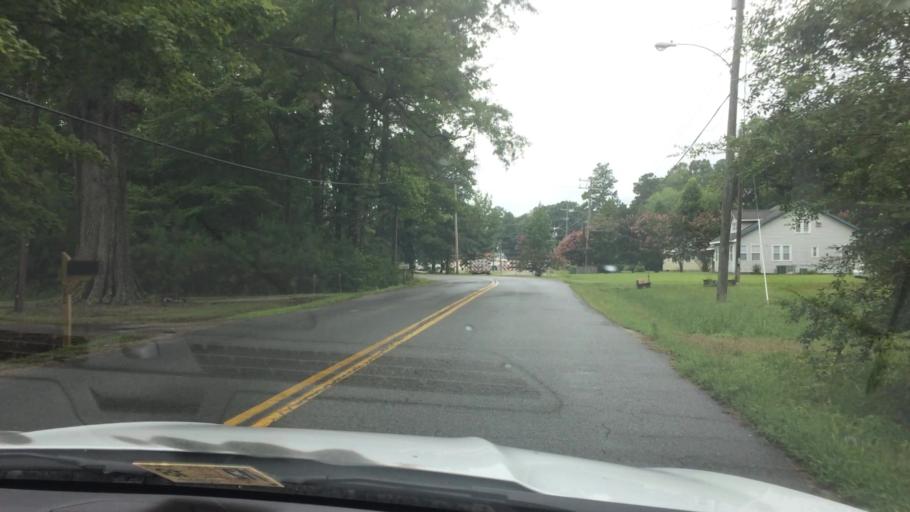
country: US
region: Virginia
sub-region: King William County
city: West Point
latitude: 37.5499
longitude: -76.8039
